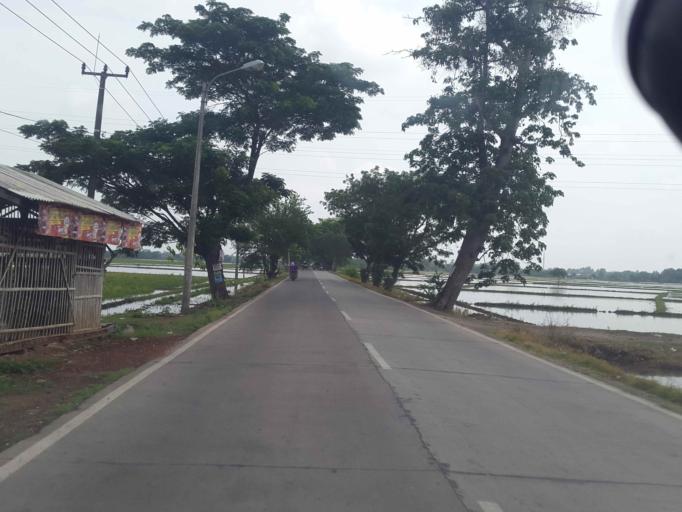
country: ID
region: West Java
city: Rengasdengklok
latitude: -6.2908
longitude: 107.3692
